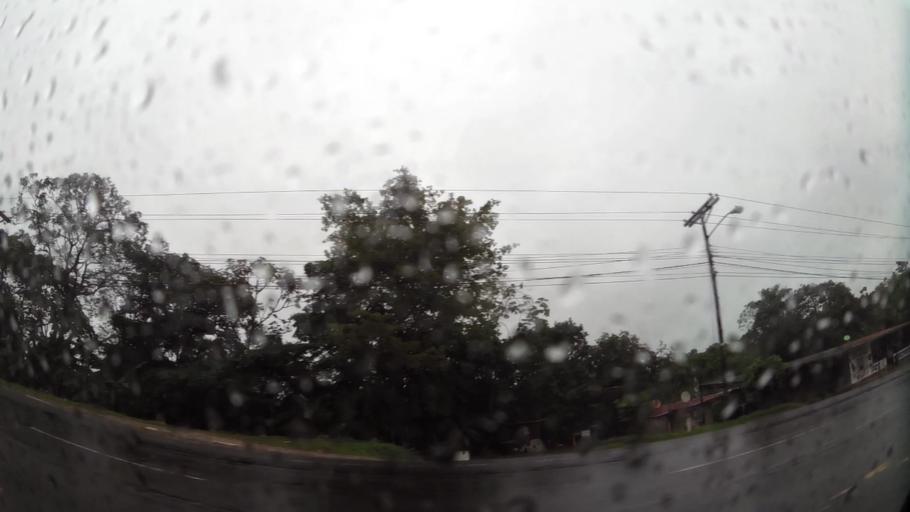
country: PA
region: Colon
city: Santa Rita Arriba
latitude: 9.3229
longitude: -79.7999
